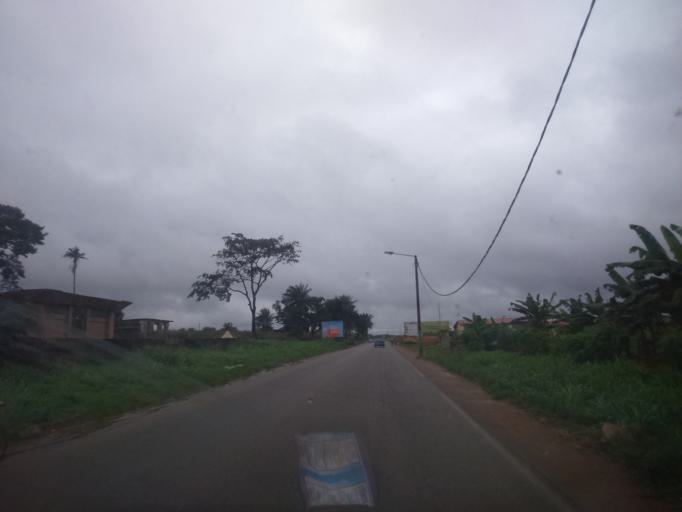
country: CI
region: Sud-Comoe
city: Bonoua
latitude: 5.2750
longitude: -3.5810
